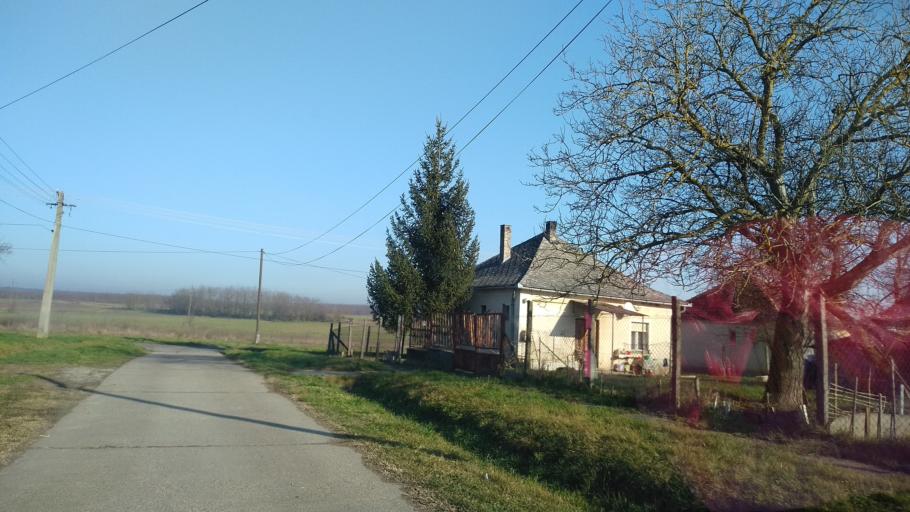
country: HU
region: Somogy
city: Barcs
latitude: 45.9651
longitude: 17.4836
